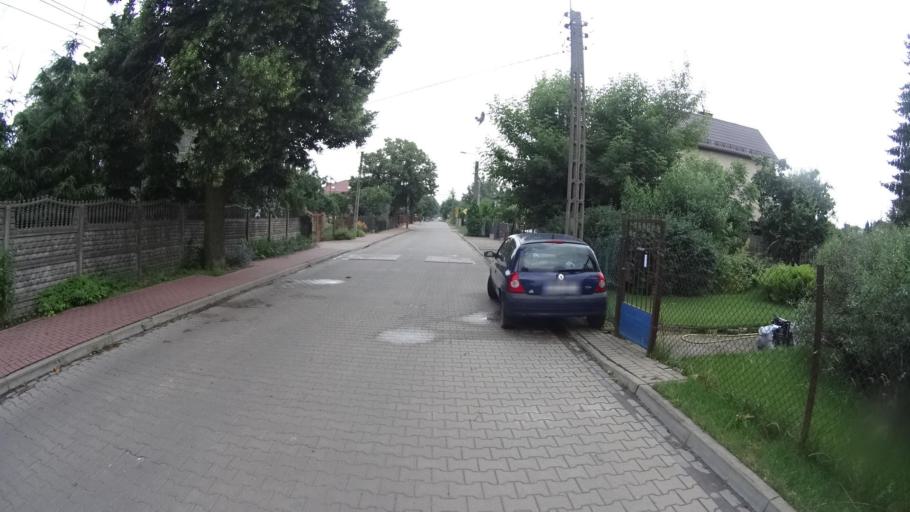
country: PL
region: Masovian Voivodeship
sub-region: Powiat pruszkowski
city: Piastow
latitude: 52.1945
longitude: 20.8524
